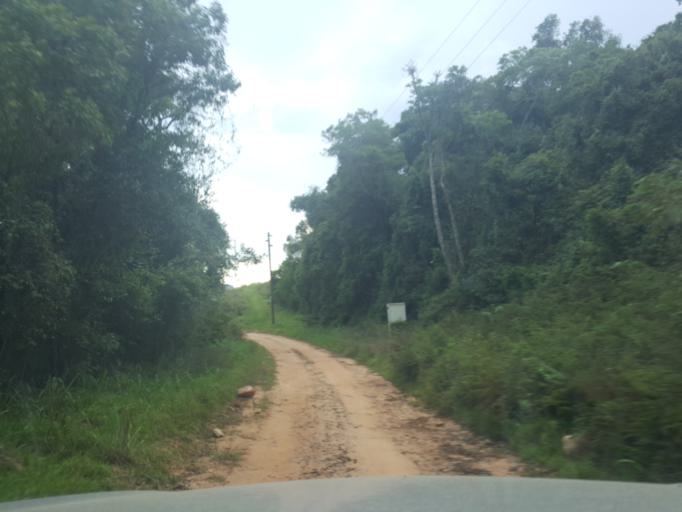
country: ZA
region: Limpopo
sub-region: Mopani District Municipality
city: Hoedspruit
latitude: -24.5790
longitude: 30.8640
